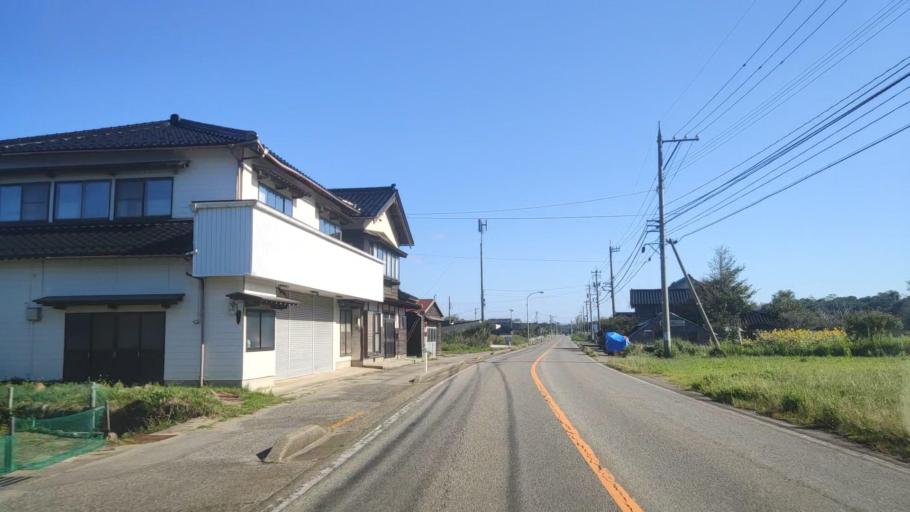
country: JP
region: Ishikawa
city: Hakui
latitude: 36.9506
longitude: 136.7654
